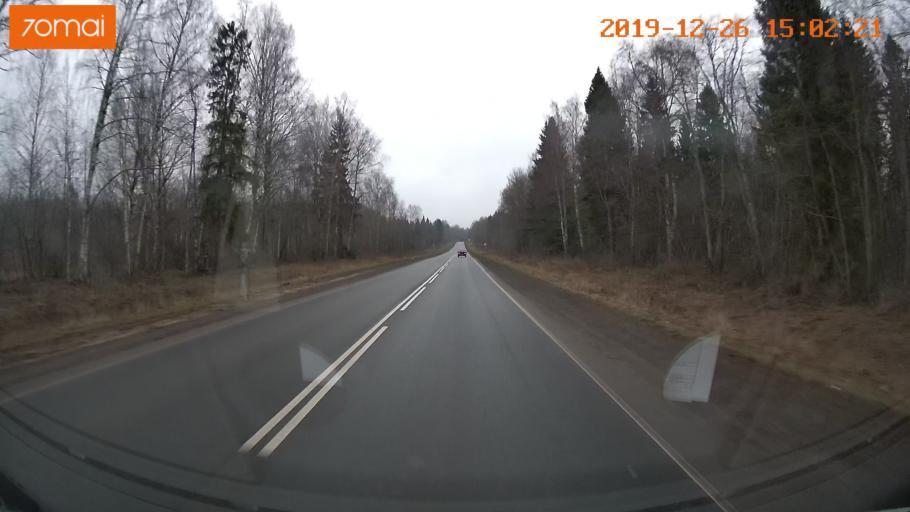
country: RU
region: Jaroslavl
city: Rybinsk
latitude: 58.2266
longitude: 38.8744
